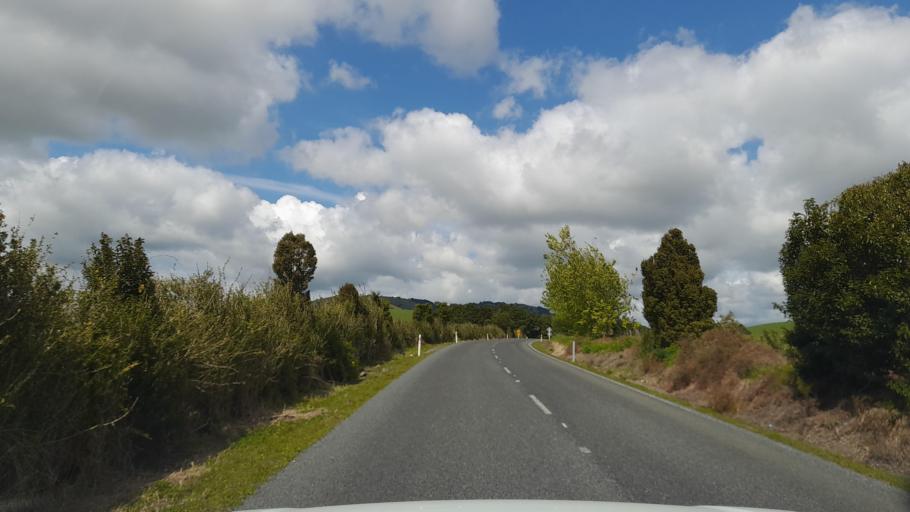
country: NZ
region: Northland
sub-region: Whangarei
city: Maungatapere
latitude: -35.6371
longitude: 174.0574
